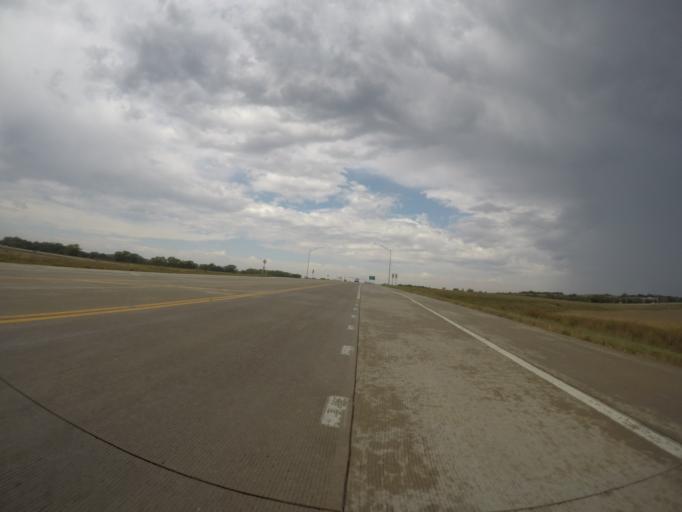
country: US
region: Kansas
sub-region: Riley County
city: Ogden
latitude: 39.1130
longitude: -96.6938
